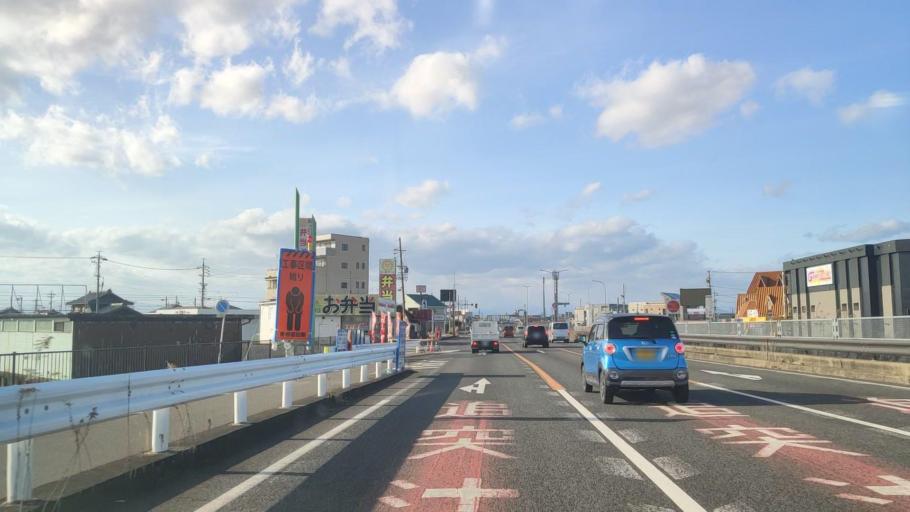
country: JP
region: Aichi
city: Kuroda
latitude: 35.3549
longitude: 136.7878
